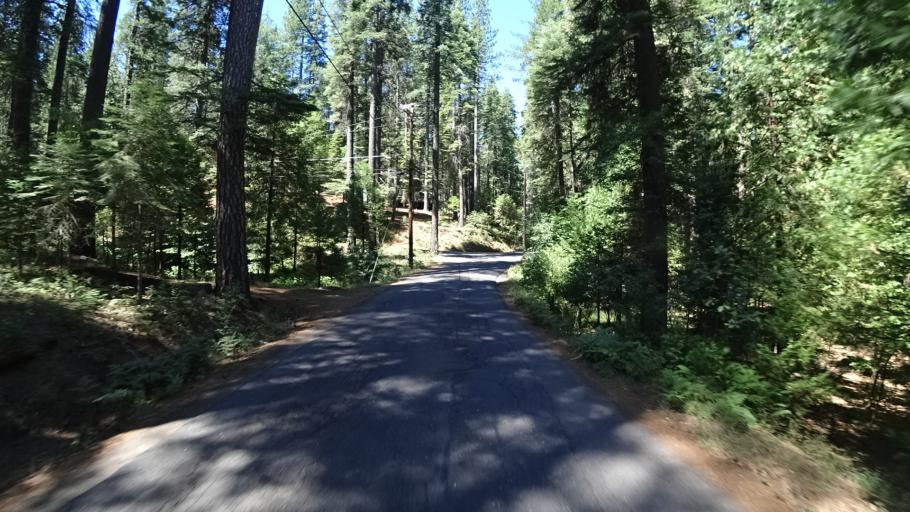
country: US
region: California
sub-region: Calaveras County
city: Arnold
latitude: 38.2341
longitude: -120.3401
